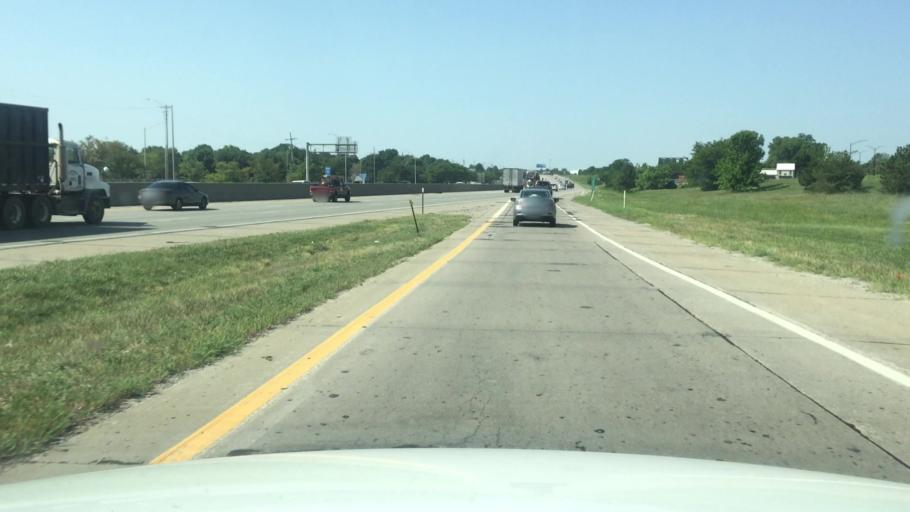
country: US
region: Kansas
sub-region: Johnson County
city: Olathe
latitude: 38.9098
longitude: -94.7753
